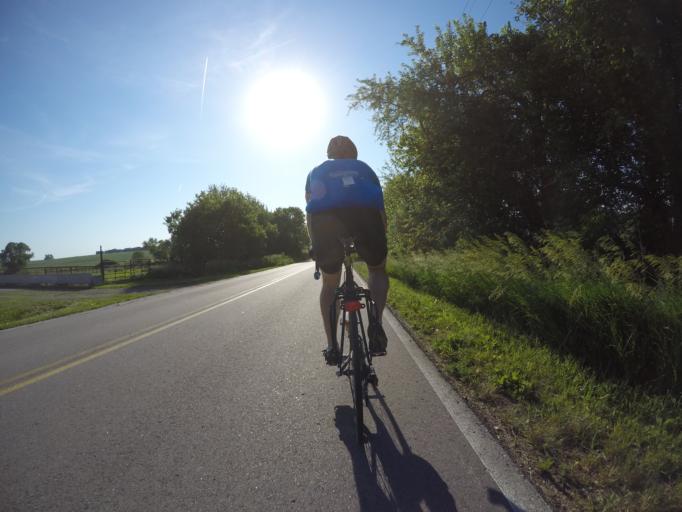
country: US
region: Nebraska
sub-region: Gage County
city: Wymore
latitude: 40.0884
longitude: -96.4992
